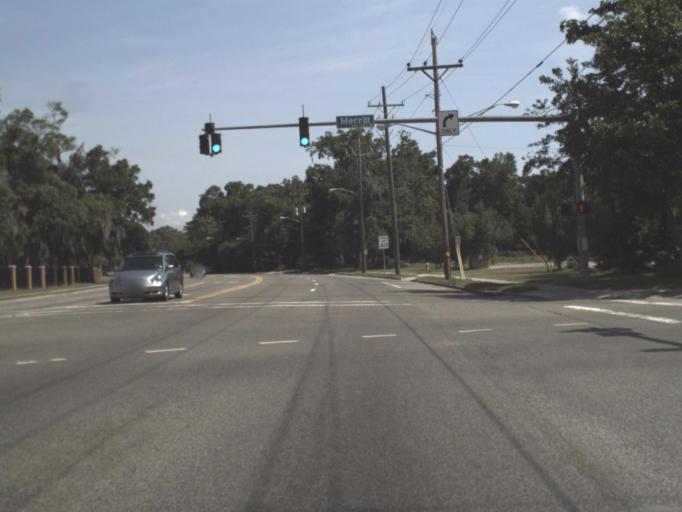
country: US
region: Florida
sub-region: Duval County
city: Jacksonville
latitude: 30.3515
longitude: -81.6026
